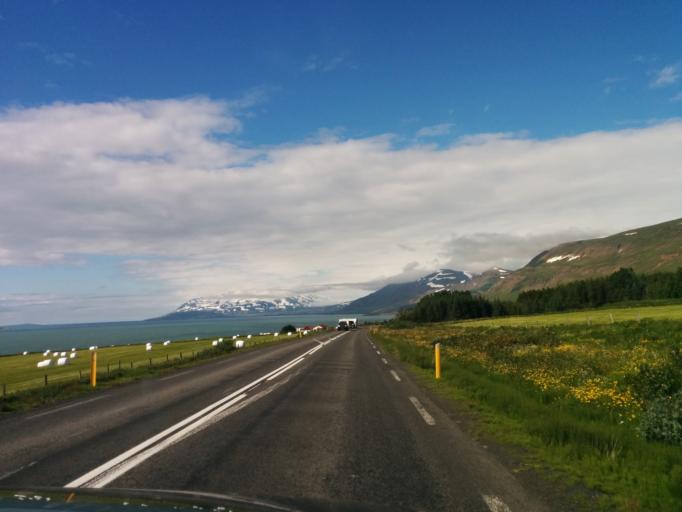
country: IS
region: Northeast
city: Akureyri
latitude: 65.7615
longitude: -18.0731
